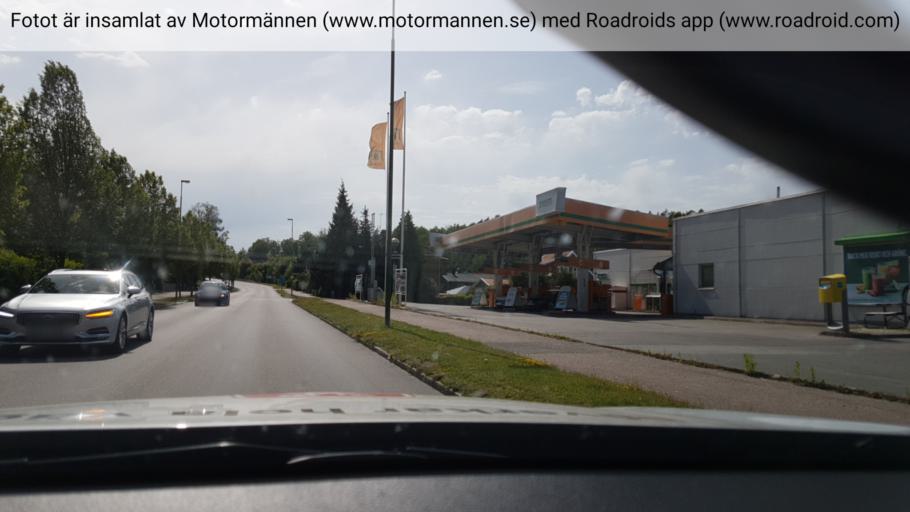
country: SE
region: Joenkoeping
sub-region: Tranas Kommun
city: Tranas
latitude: 58.0288
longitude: 14.9635
